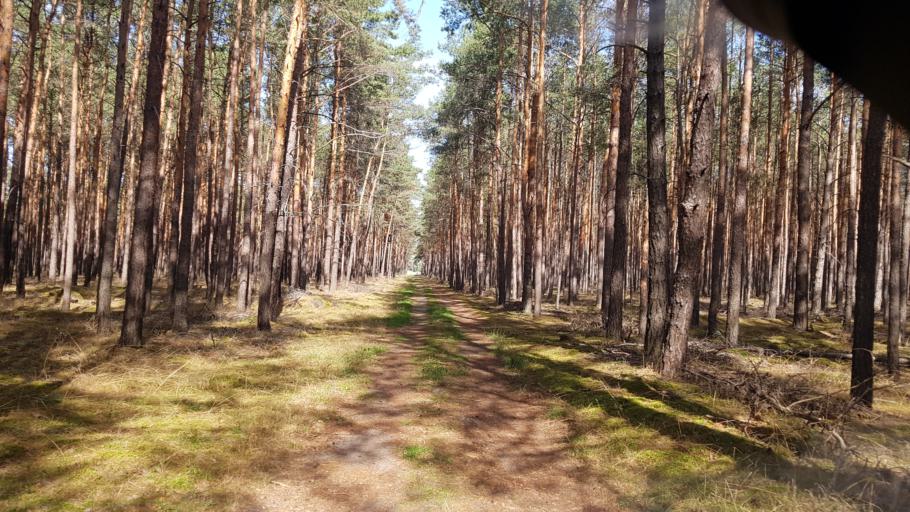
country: DE
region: Brandenburg
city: Sonnewalde
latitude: 51.6544
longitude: 13.6390
